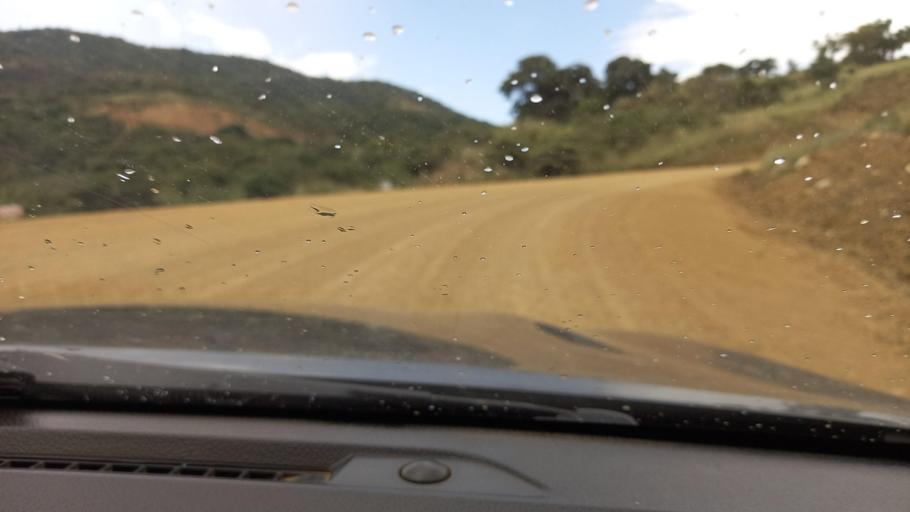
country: ET
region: Southern Nations, Nationalities, and People's Region
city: Mizan Teferi
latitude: 6.2038
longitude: 35.6705
